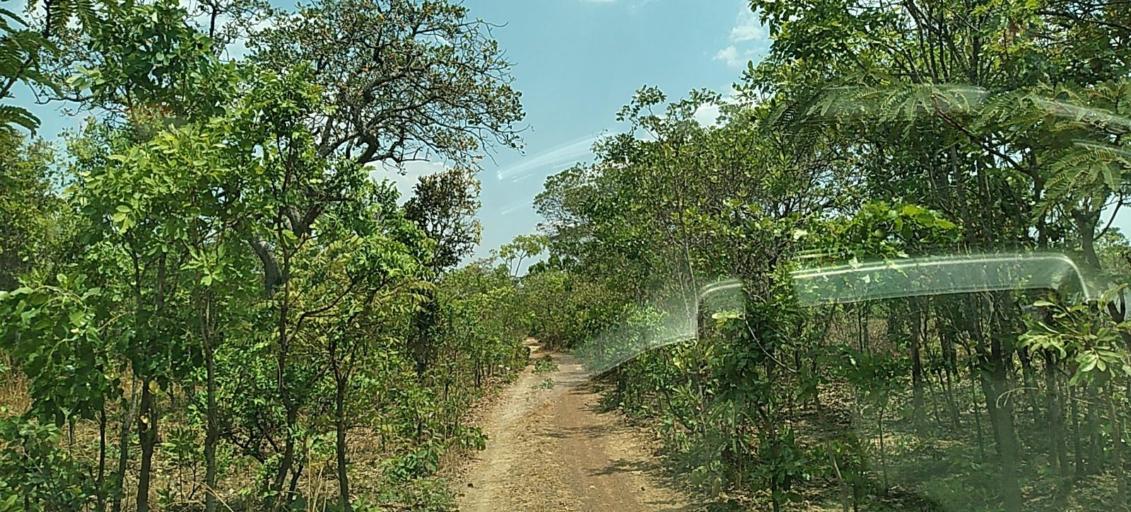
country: CD
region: Katanga
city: Kipushi
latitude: -11.9772
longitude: 27.4145
